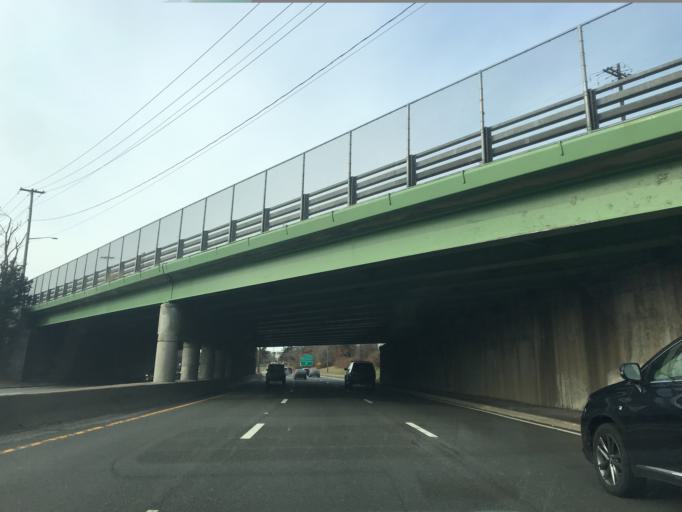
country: US
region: New York
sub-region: Nassau County
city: East Garden City
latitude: 40.7365
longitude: -73.5884
